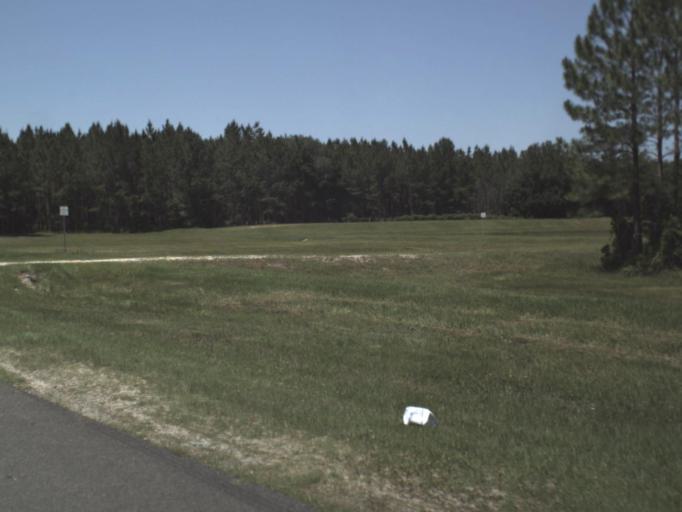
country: US
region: Florida
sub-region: Clay County
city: Lakeside
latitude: 30.1828
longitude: -81.8358
